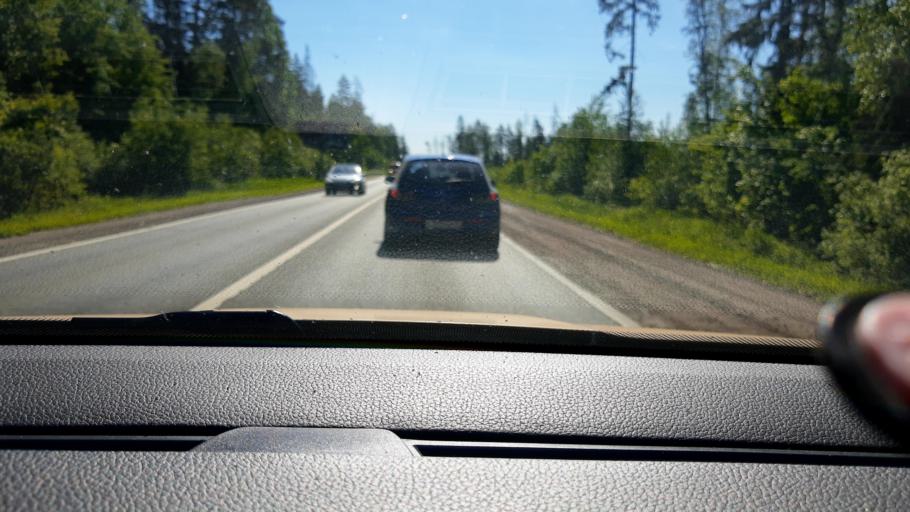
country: RU
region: Moskovskaya
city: Pavlovskaya Sloboda
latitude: 55.7973
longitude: 37.1392
